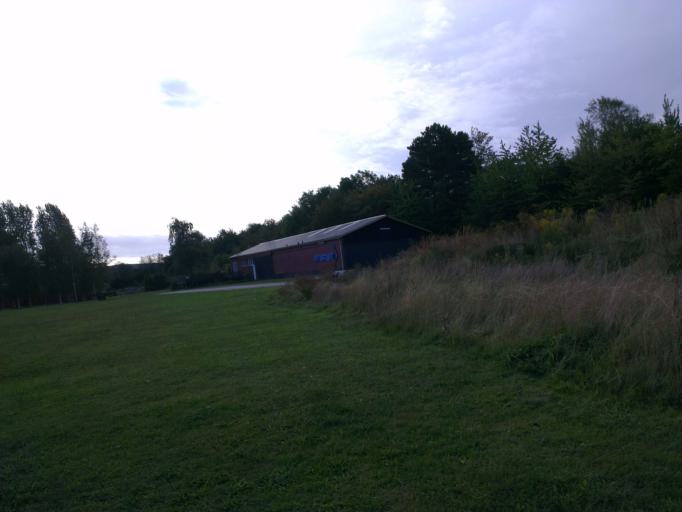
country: DK
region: Capital Region
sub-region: Frederikssund Kommune
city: Frederikssund
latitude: 55.8522
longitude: 12.0679
